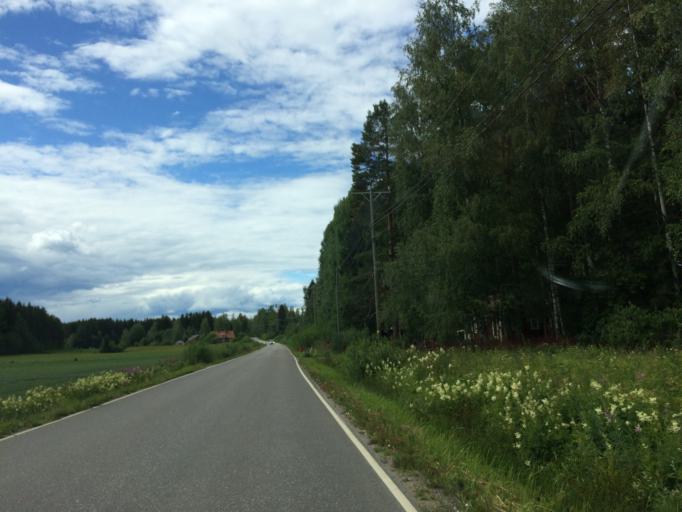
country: FI
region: Haeme
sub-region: Haemeenlinna
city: Tervakoski
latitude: 60.8340
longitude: 24.5820
